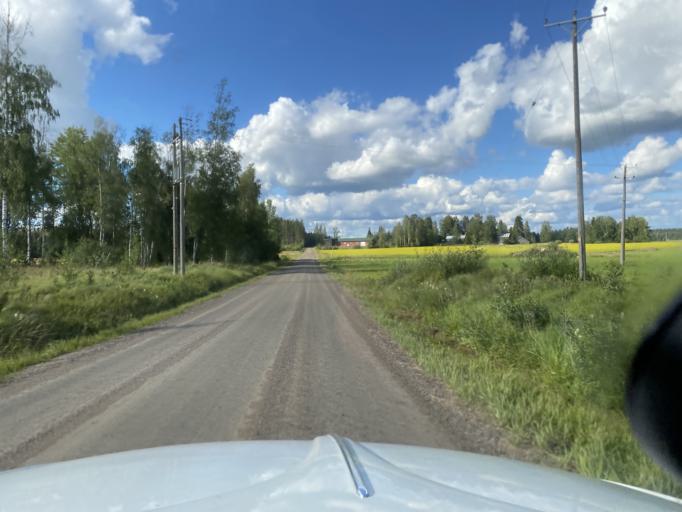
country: FI
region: Pirkanmaa
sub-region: Lounais-Pirkanmaa
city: Punkalaidun
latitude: 61.1119
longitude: 23.2745
